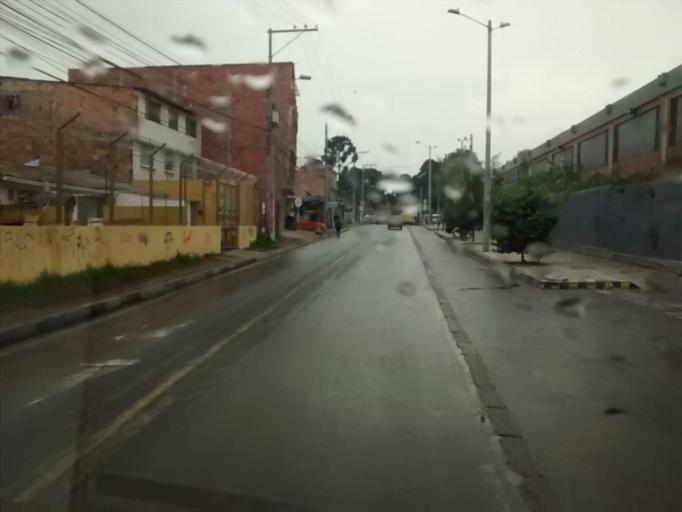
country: CO
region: Cundinamarca
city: Cota
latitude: 4.7562
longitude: -74.0925
